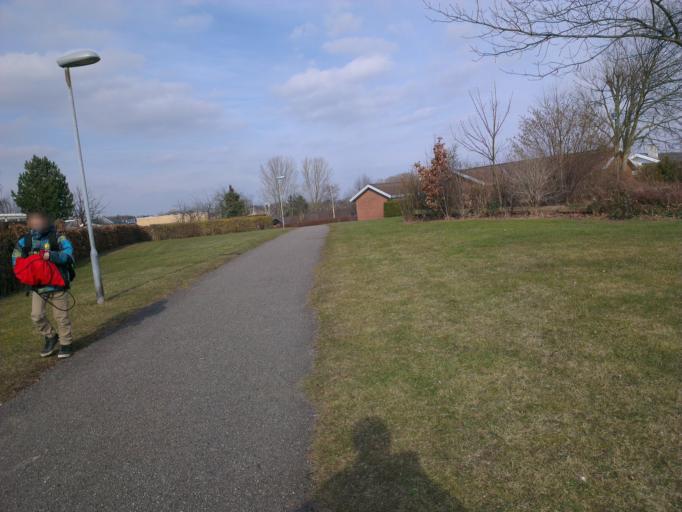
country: DK
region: Capital Region
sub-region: Frederikssund Kommune
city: Frederikssund
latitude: 55.8281
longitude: 12.0848
